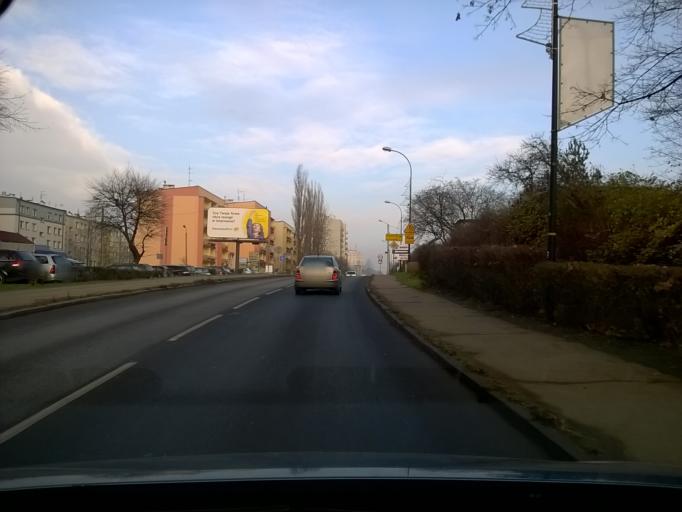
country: PL
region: Silesian Voivodeship
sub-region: Swietochlowice
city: Swietochlowice
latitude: 50.2607
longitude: 18.9359
